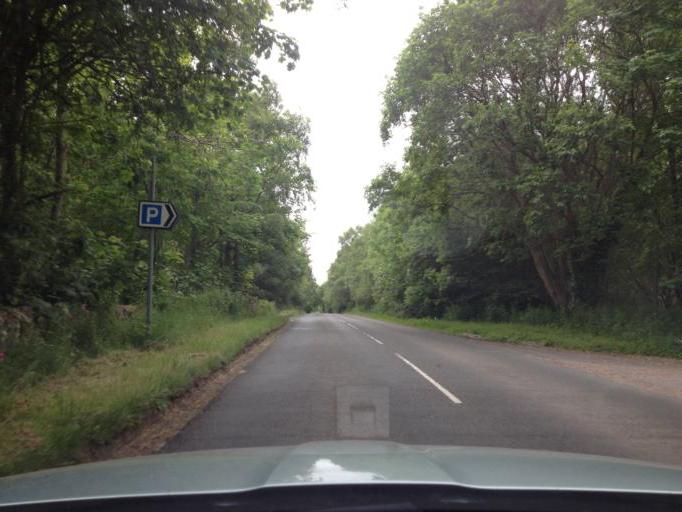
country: GB
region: Scotland
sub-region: Fife
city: Strathkinness
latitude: 56.3260
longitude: -2.8757
